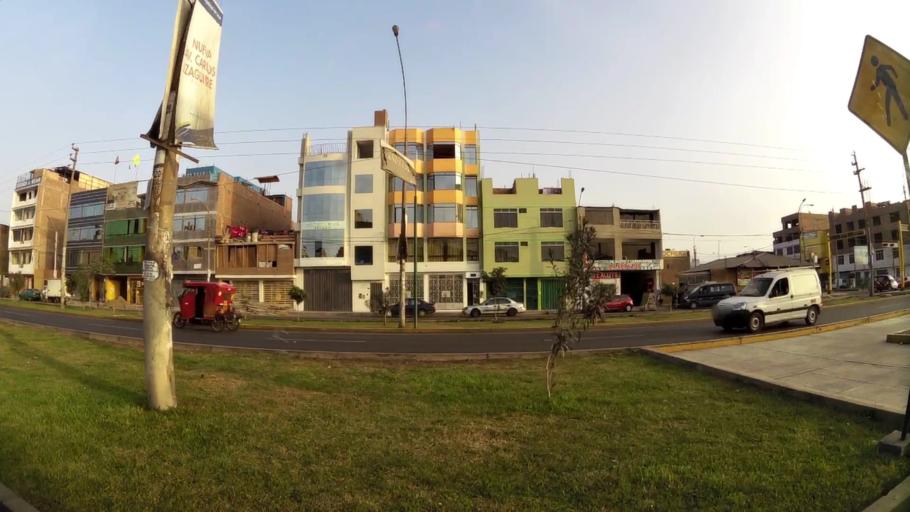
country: PE
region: Lima
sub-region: Lima
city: Independencia
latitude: -11.9907
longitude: -77.0926
